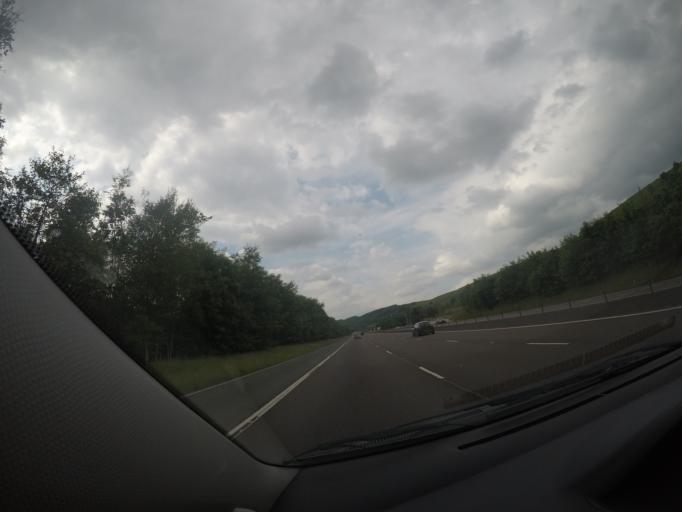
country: GB
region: Scotland
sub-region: Dumfries and Galloway
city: Moffat
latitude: 55.3329
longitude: -3.4789
